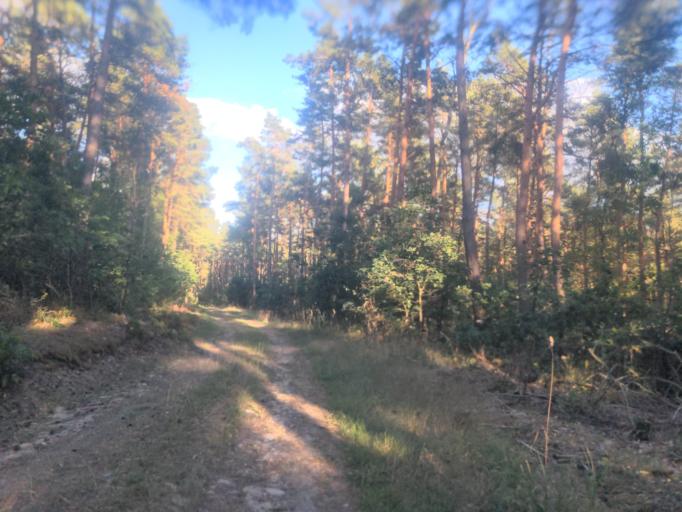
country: DE
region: Lower Saxony
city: Neu Darchau
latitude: 53.2191
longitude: 10.8602
